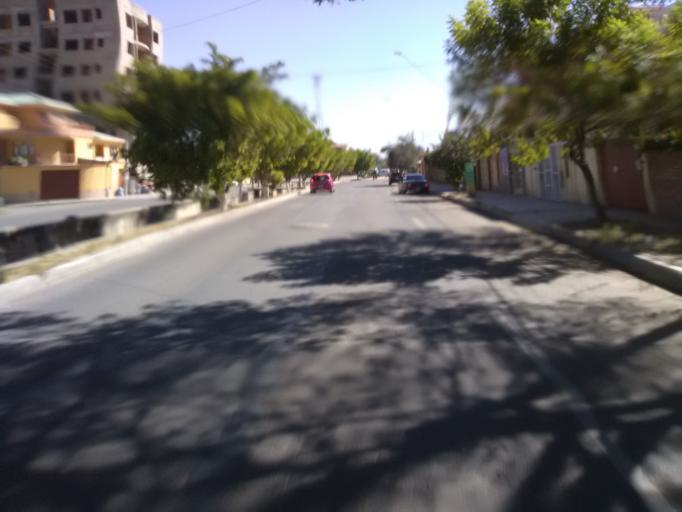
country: BO
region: Cochabamba
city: Cochabamba
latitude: -17.3819
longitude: -66.1934
